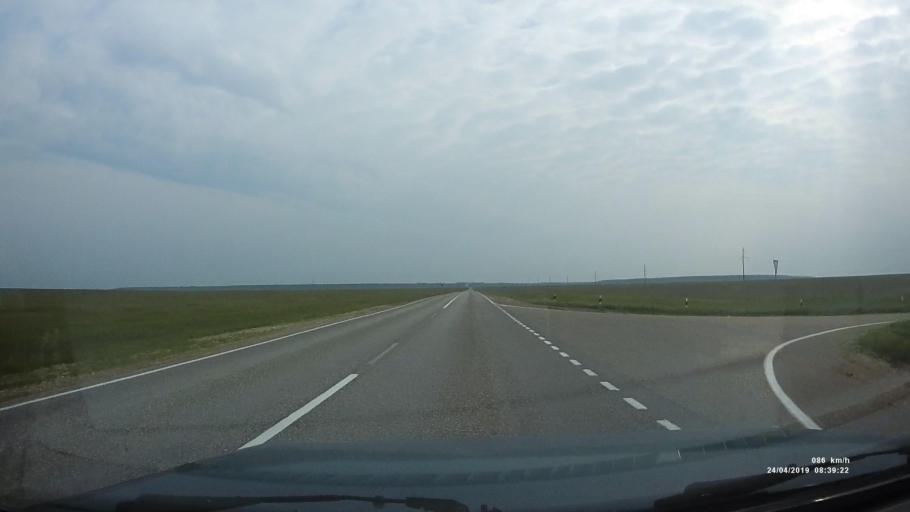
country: RU
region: Kalmykiya
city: Arshan'
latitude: 46.2204
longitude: 43.9827
